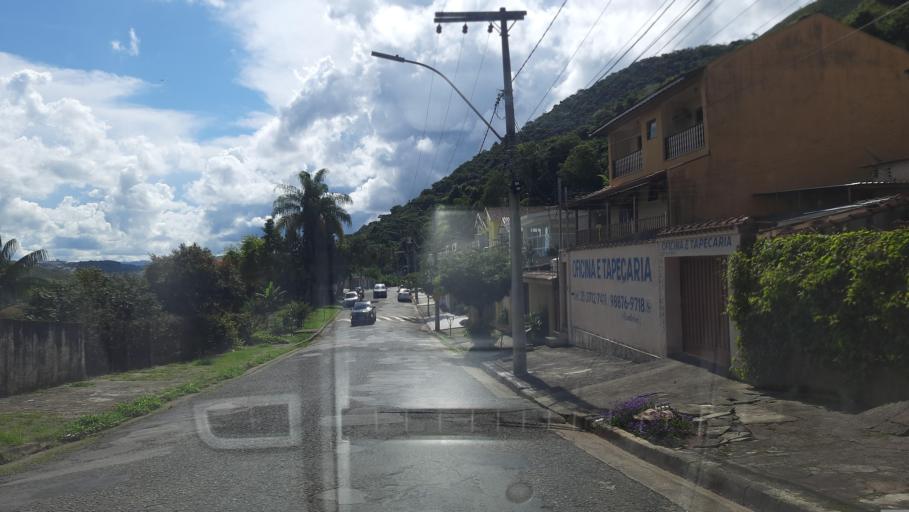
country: BR
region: Minas Gerais
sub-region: Pocos De Caldas
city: Pocos de Caldas
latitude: -21.7780
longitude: -46.5628
